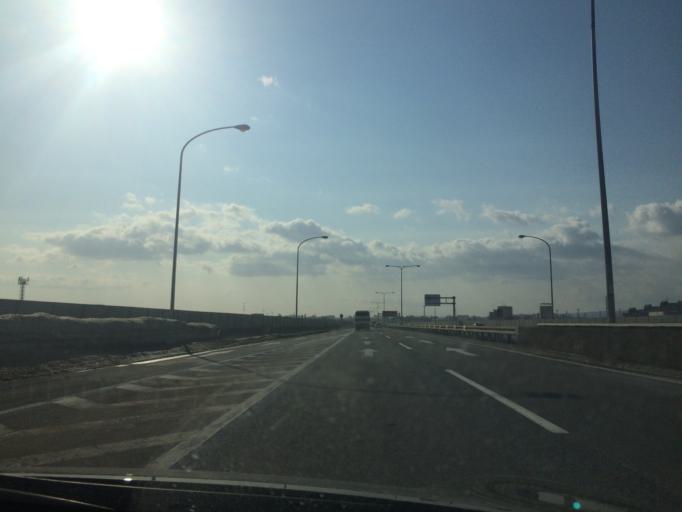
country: JP
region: Hokkaido
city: Sapporo
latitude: 43.0582
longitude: 141.4261
